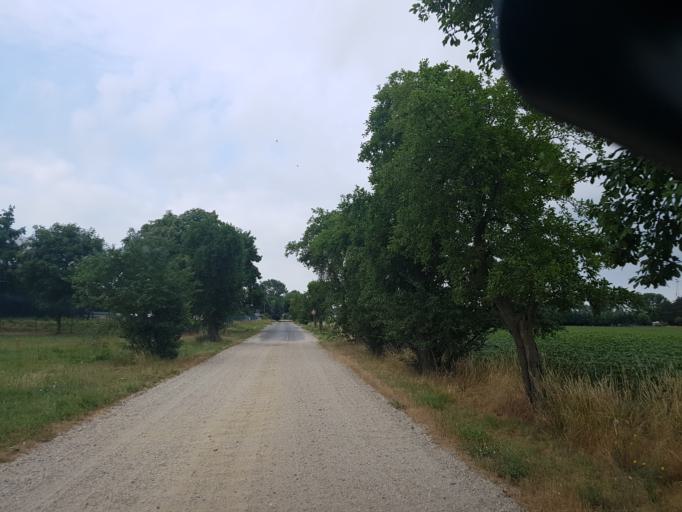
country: DE
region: Brandenburg
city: Doberlug-Kirchhain
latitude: 51.6942
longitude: 13.5191
